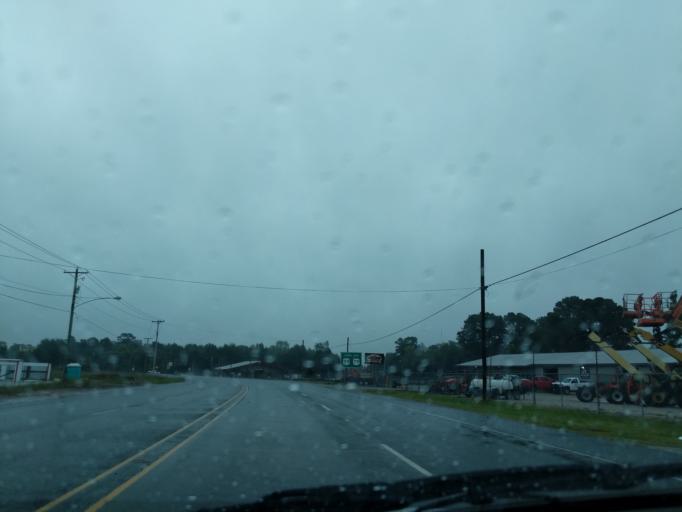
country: US
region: Texas
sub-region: Panola County
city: Carthage
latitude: 32.1574
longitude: -94.3271
